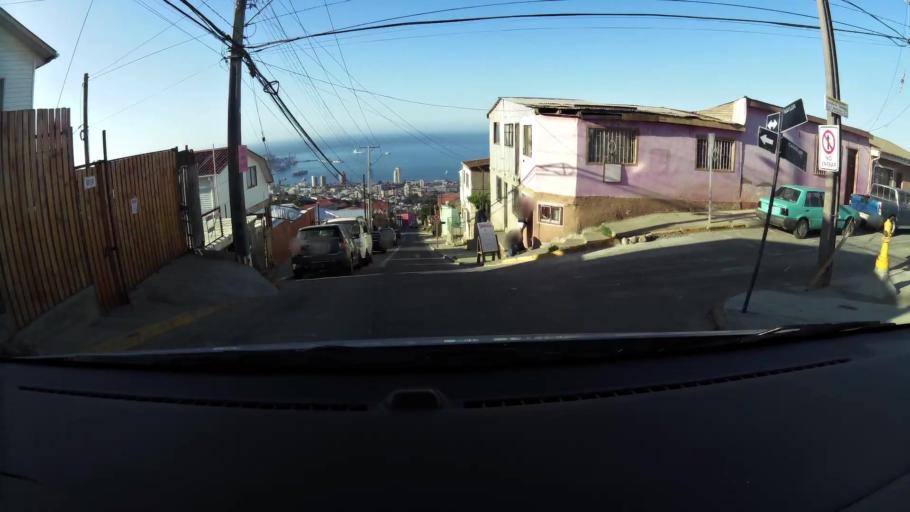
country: CL
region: Valparaiso
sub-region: Provincia de Valparaiso
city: Valparaiso
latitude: -33.0596
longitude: -71.6128
